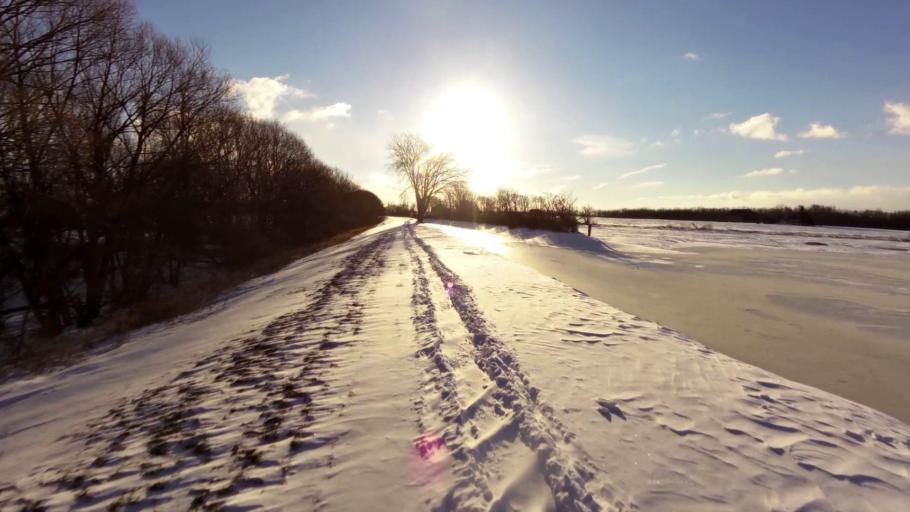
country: US
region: New York
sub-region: Orleans County
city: Albion
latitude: 43.2480
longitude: -78.2839
